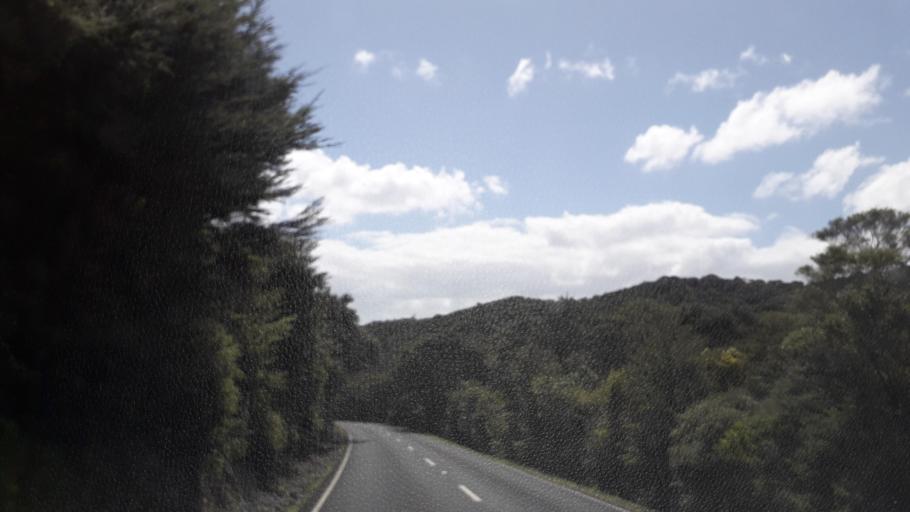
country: NZ
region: Northland
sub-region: Far North District
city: Paihia
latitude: -35.2504
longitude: 174.2603
